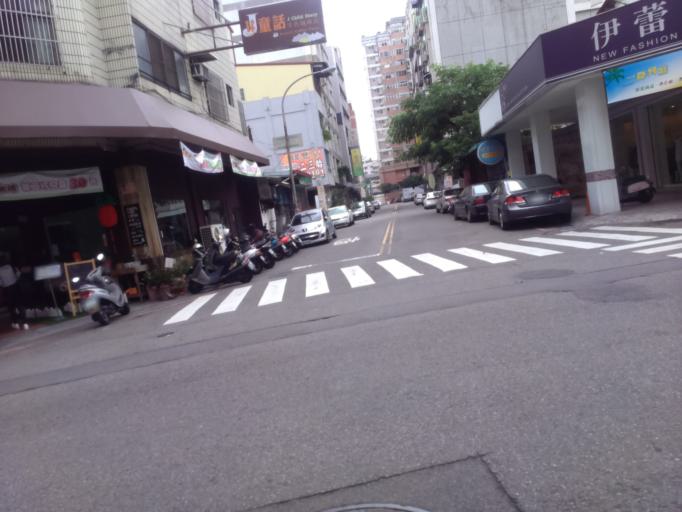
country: TW
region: Taiwan
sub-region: Taichung City
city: Taichung
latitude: 24.1712
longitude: 120.6783
